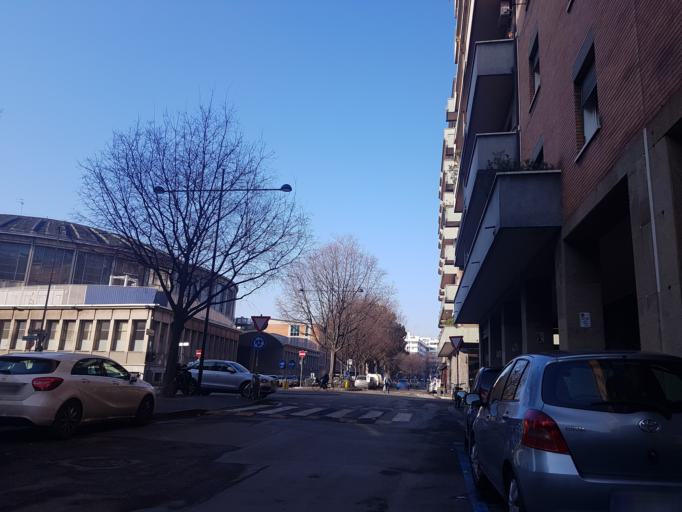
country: IT
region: Emilia-Romagna
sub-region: Provincia di Bologna
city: Bologna
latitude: 44.5002
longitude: 11.3335
